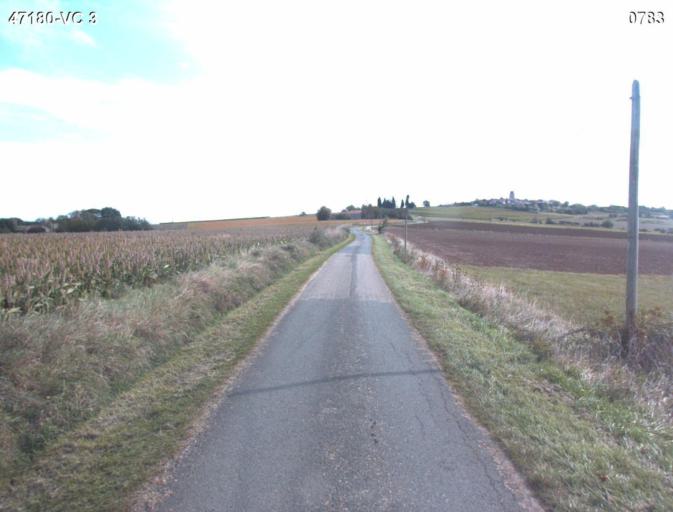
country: FR
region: Aquitaine
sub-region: Departement du Lot-et-Garonne
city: Sainte-Colombe-en-Bruilhois
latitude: 44.1602
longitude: 0.4472
